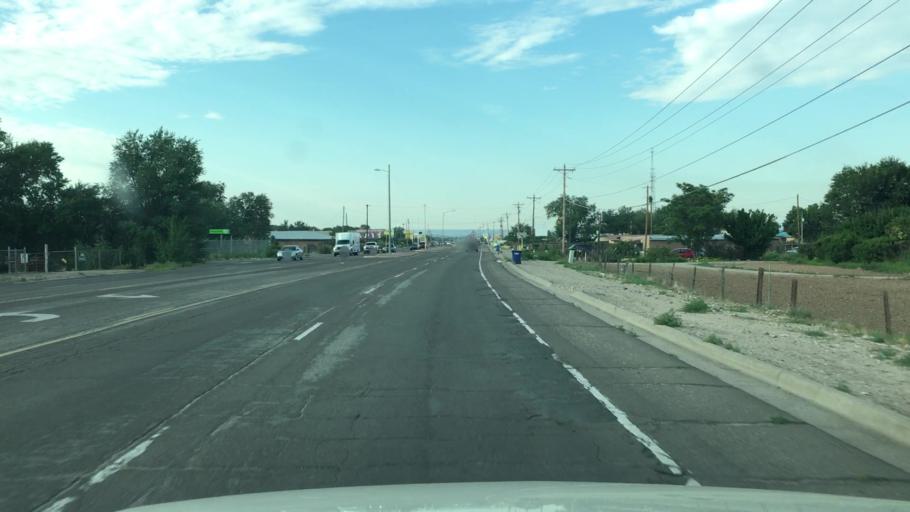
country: US
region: New Mexico
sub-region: Rio Arriba County
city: Ohkay Owingeh
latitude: 36.0235
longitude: -106.0638
